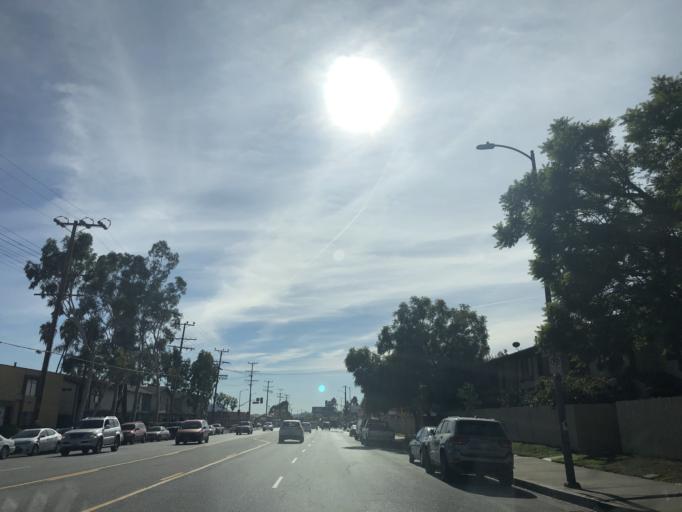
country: US
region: California
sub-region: Los Angeles County
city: North Hollywood
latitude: 34.2264
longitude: -118.3660
